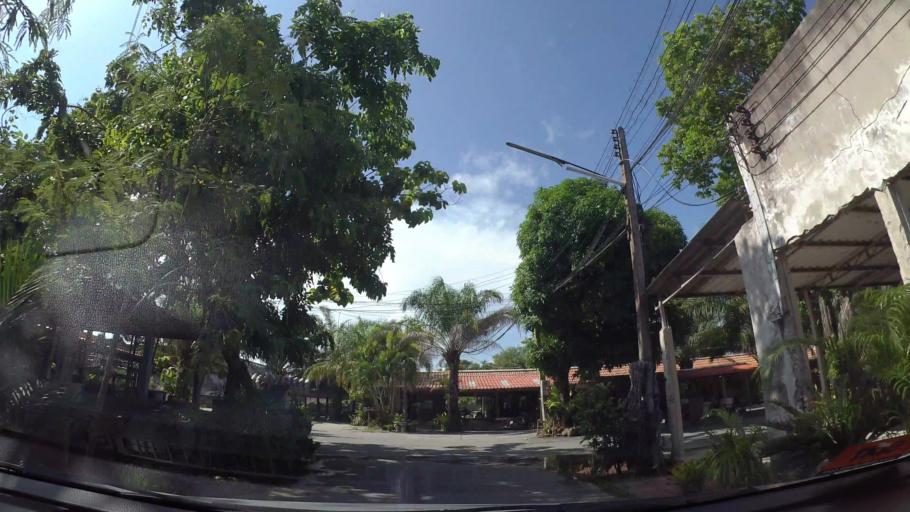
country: TH
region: Rayong
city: Rayong
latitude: 12.6748
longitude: 101.2918
